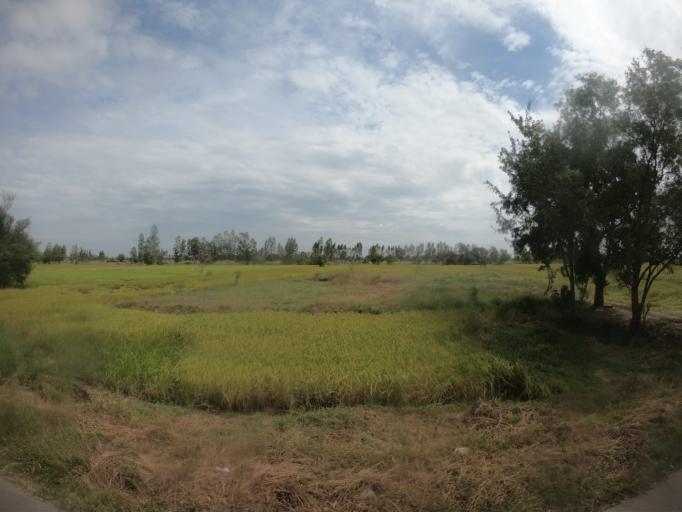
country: TH
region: Maha Sarakham
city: Chiang Yuen
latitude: 16.3781
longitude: 103.1041
